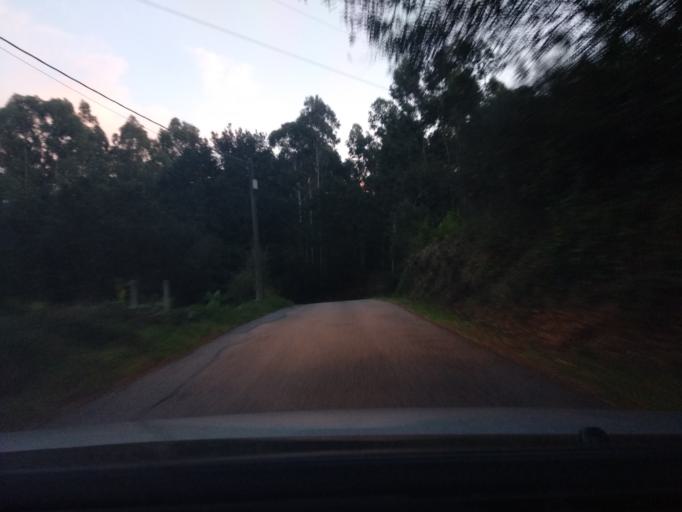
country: ES
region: Galicia
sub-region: Provincia de Pontevedra
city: Moana
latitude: 42.3007
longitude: -8.6976
